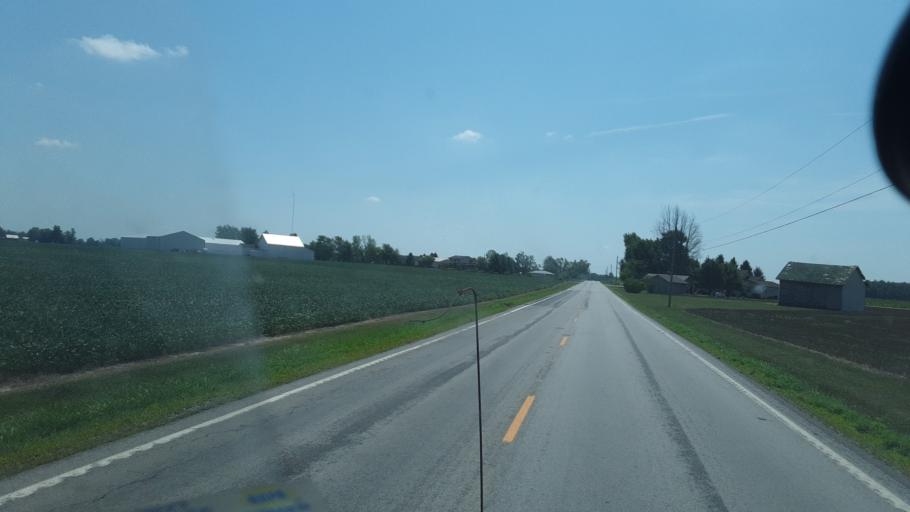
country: US
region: Ohio
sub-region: Hancock County
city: Arlington
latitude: 40.9372
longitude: -83.5708
